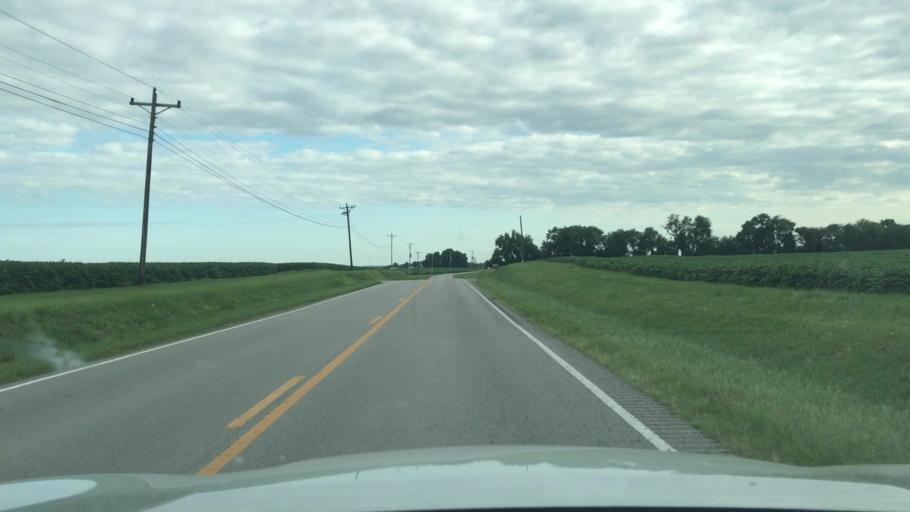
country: US
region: Kentucky
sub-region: Todd County
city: Elkton
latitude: 36.7684
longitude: -87.1668
